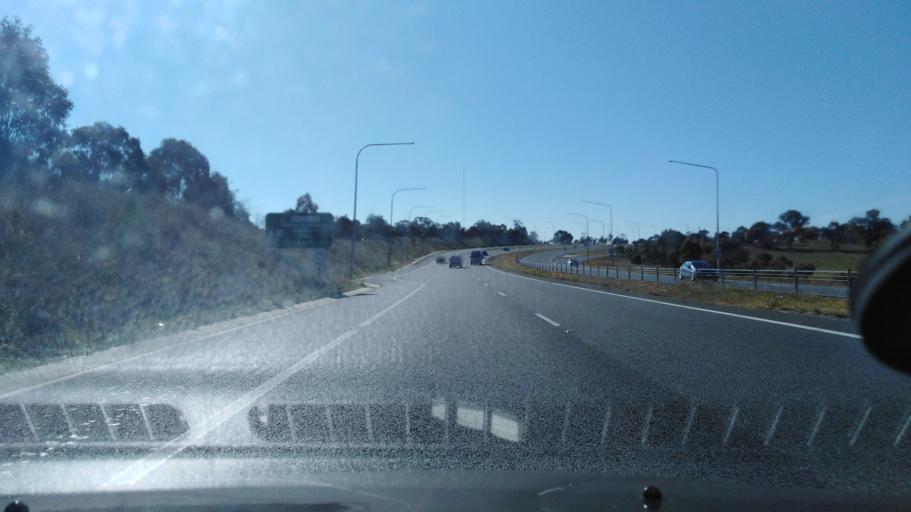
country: AU
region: Australian Capital Territory
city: Kaleen
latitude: -35.2303
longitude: 149.1184
